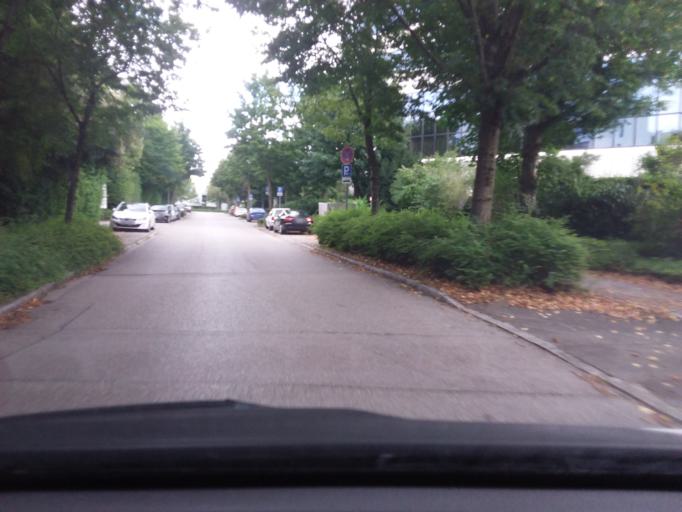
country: DE
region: Bavaria
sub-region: Upper Bavaria
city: Unterschleissheim
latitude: 48.2876
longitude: 11.5686
